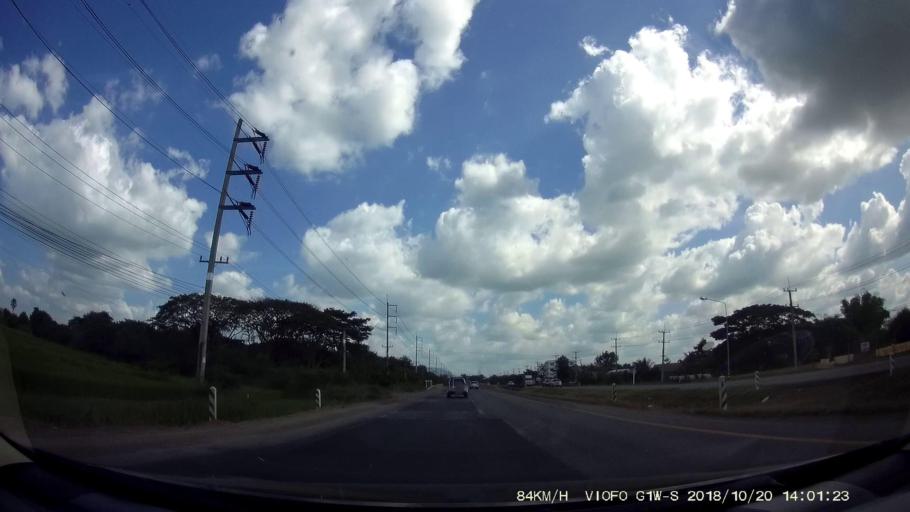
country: TH
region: Khon Kaen
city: Chum Phae
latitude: 16.5027
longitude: 102.1200
